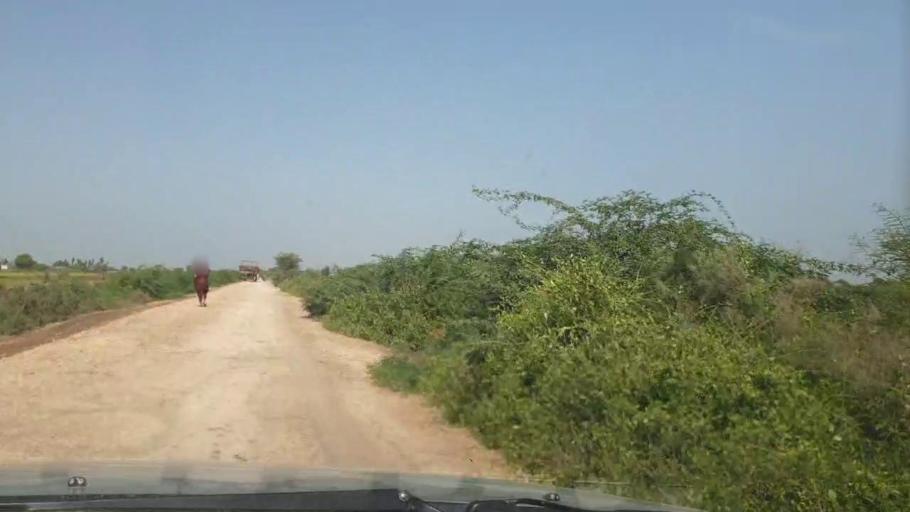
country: PK
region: Sindh
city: Tando Ghulam Ali
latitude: 25.0750
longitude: 68.8020
